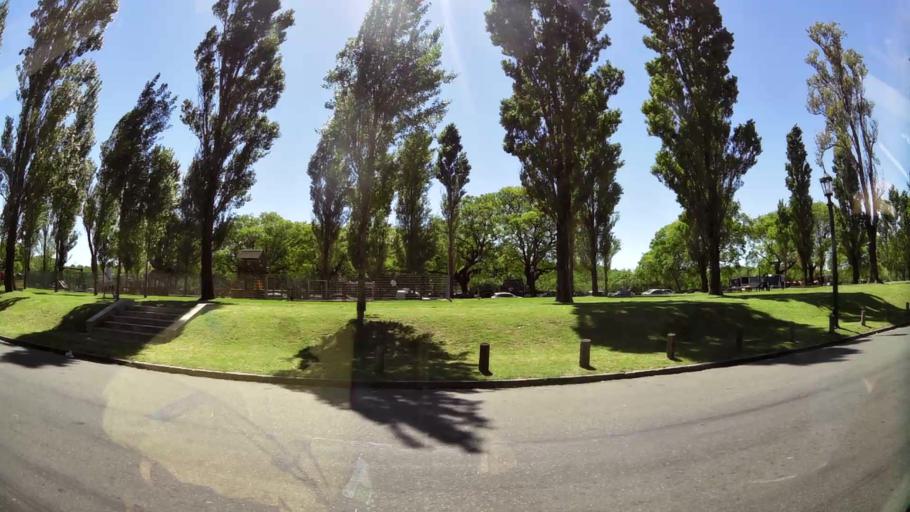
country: AR
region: Buenos Aires F.D.
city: Buenos Aires
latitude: -34.5995
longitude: -58.3629
